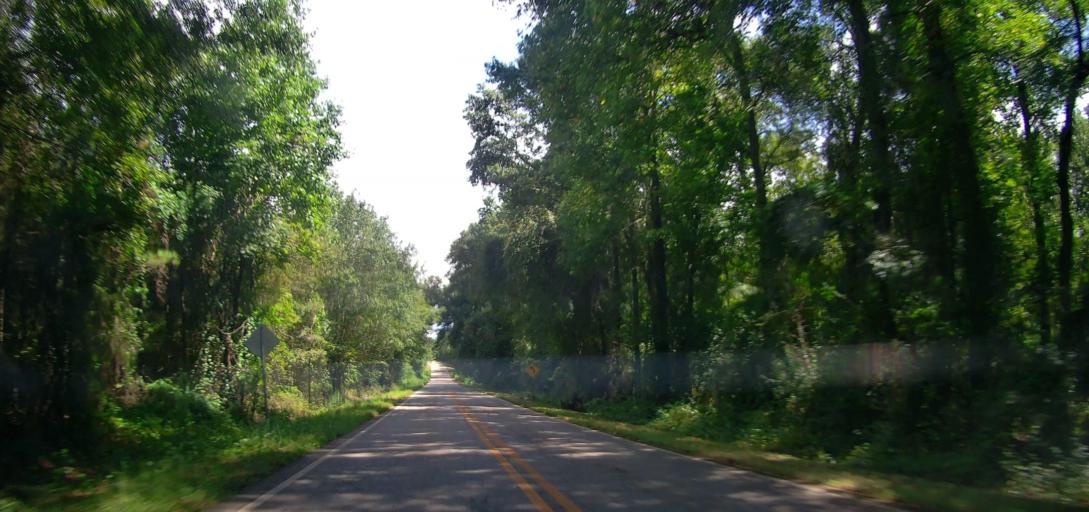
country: US
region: Georgia
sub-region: Peach County
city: Fort Valley
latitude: 32.5347
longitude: -83.8128
